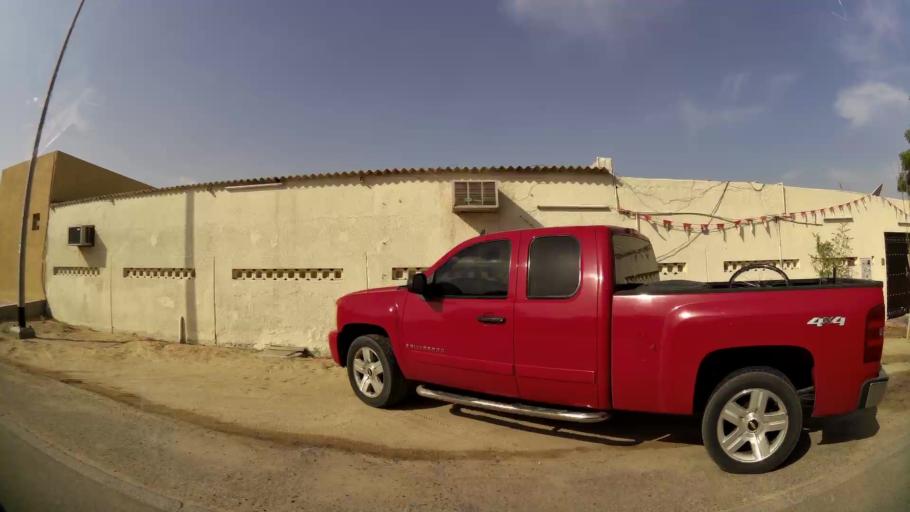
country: AE
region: Ash Shariqah
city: Sharjah
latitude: 25.2223
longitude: 55.4003
